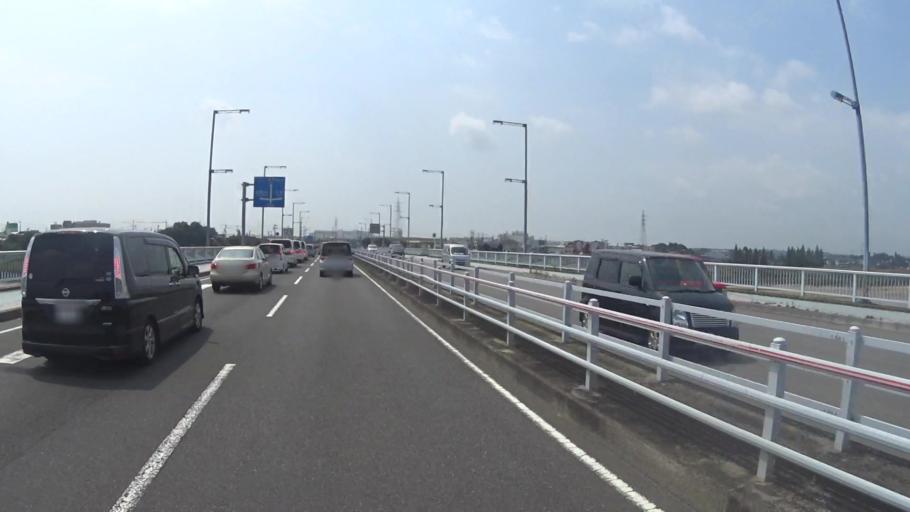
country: JP
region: Mie
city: Suzuka
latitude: 34.8764
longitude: 136.5223
